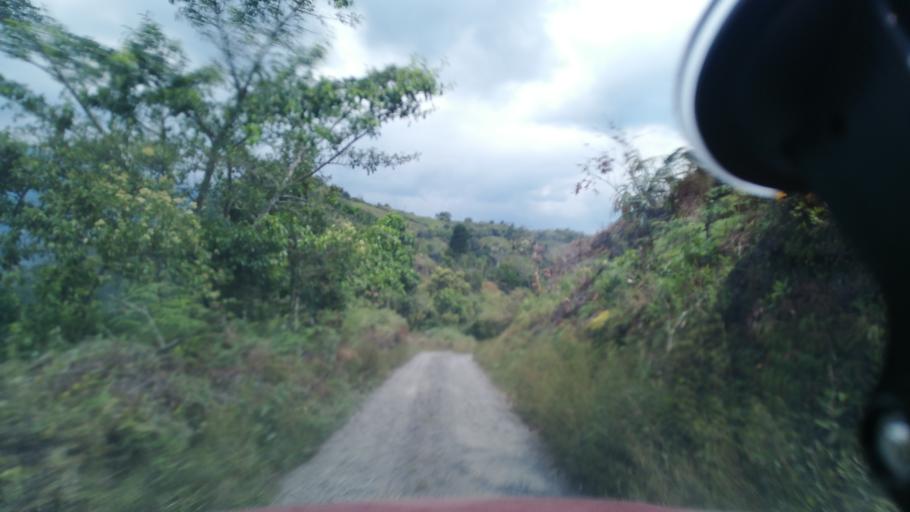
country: CO
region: Cundinamarca
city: Vergara
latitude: 5.1878
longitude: -74.2733
